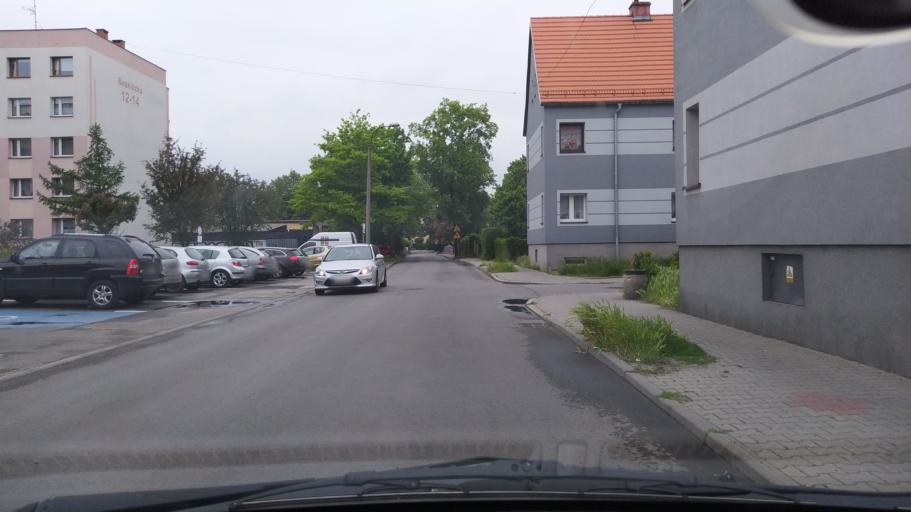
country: PL
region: Silesian Voivodeship
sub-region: Powiat gliwicki
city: Przyszowice
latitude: 50.2931
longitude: 18.7367
